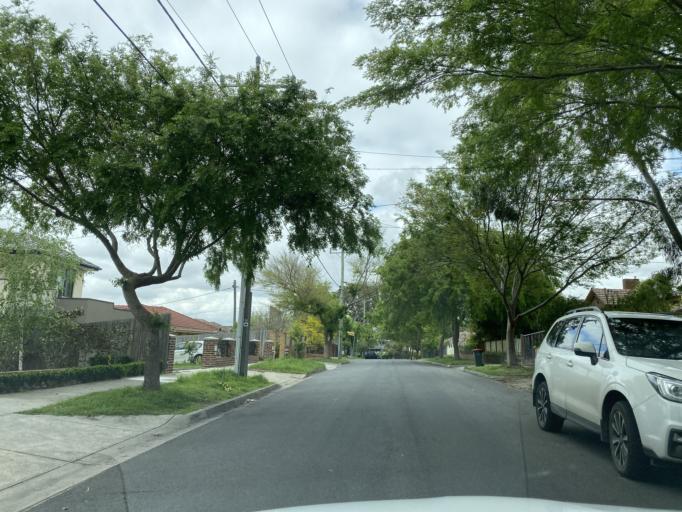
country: AU
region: Victoria
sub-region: Whitehorse
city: Box Hill South
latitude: -37.8368
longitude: 145.1180
